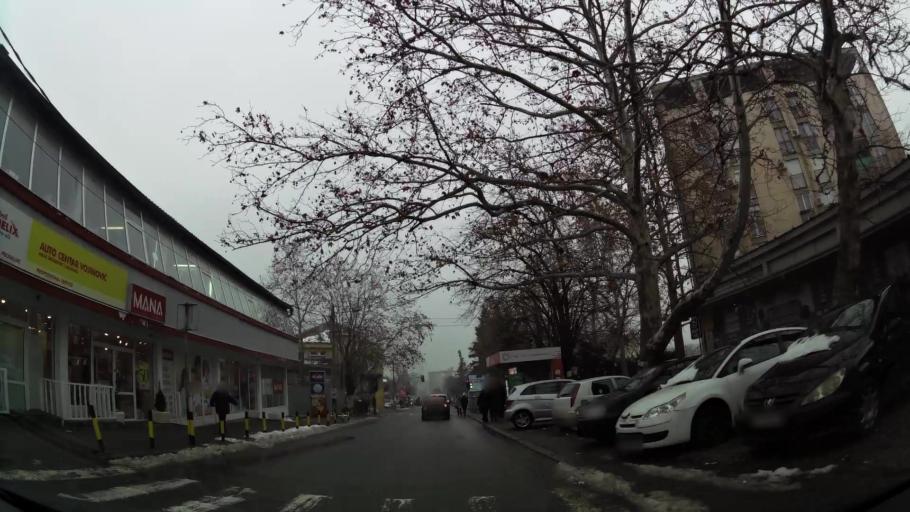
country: RS
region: Central Serbia
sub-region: Belgrade
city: Vozdovac
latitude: 44.7714
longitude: 20.4823
